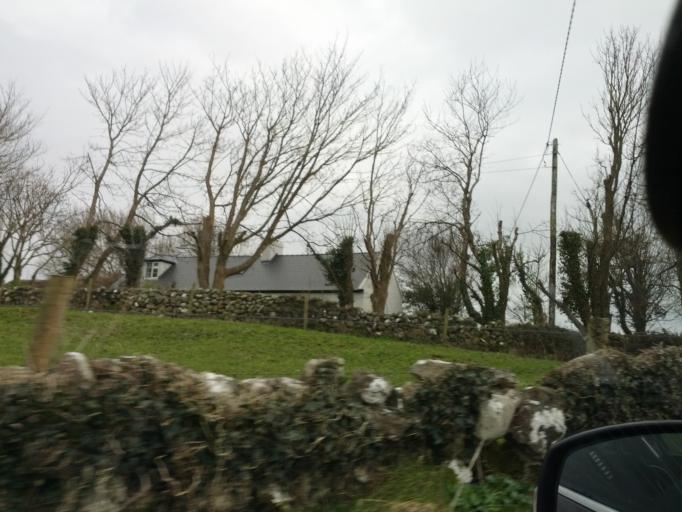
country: IE
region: Connaught
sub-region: County Galway
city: Oranmore
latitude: 53.2051
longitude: -8.9122
